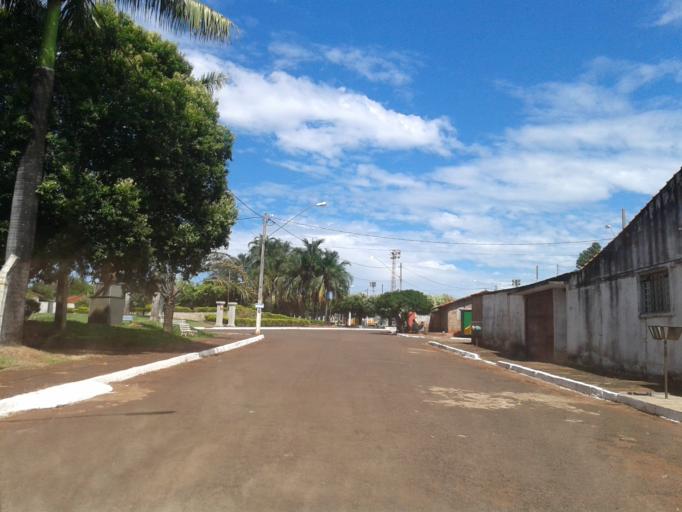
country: BR
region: Minas Gerais
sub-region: Capinopolis
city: Capinopolis
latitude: -18.5165
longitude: -49.5018
